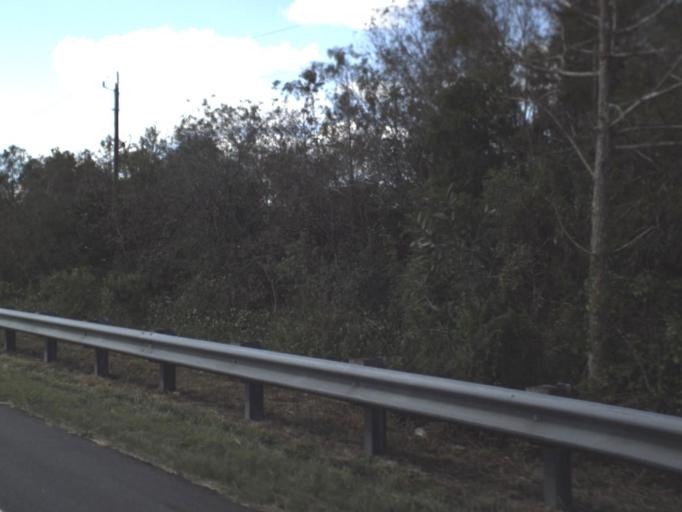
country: US
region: Florida
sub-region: Miami-Dade County
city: Kendall West
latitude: 25.8589
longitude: -81.0533
